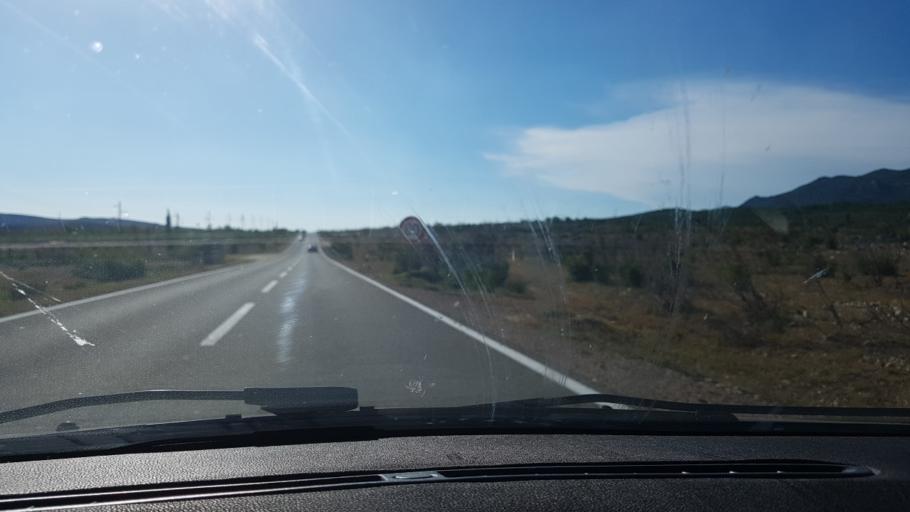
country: HR
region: Zadarska
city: Krusevo
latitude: 44.2242
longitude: 15.6408
